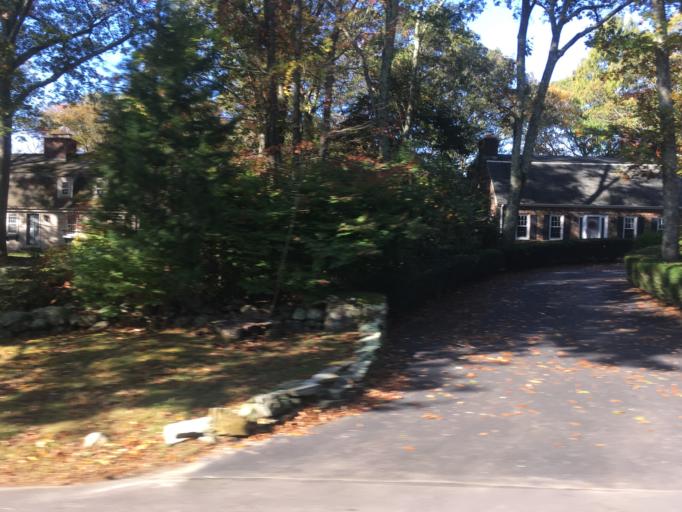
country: US
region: Rhode Island
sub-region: Kent County
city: East Greenwich
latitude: 41.6563
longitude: -71.4762
